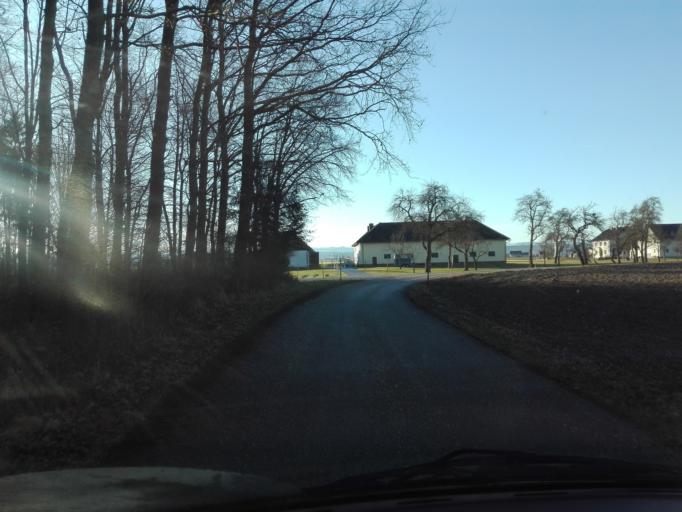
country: AT
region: Upper Austria
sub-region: Politischer Bezirk Perg
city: Perg
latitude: 48.2038
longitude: 14.6772
